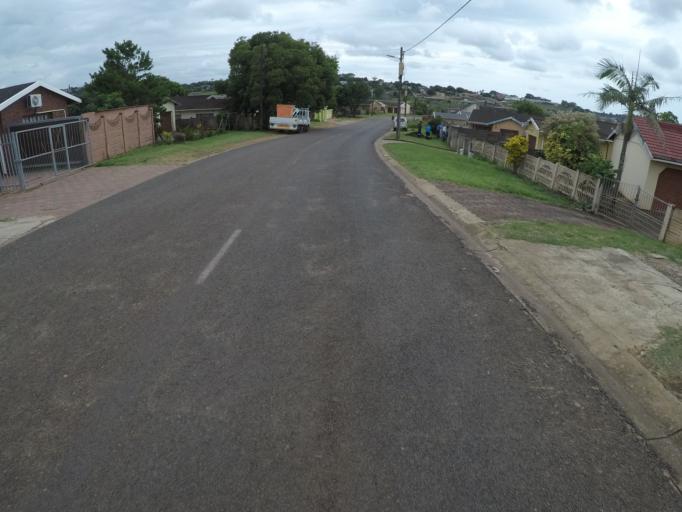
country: ZA
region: KwaZulu-Natal
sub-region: uThungulu District Municipality
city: Empangeni
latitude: -28.7781
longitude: 31.8553
